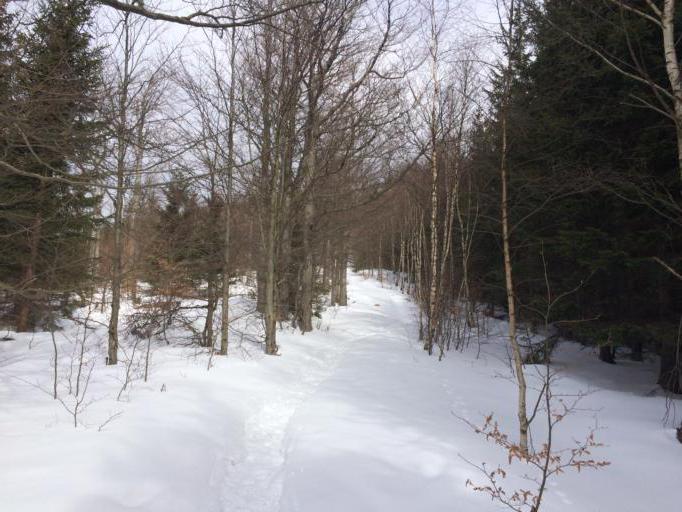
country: CZ
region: Olomoucky
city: Vapenna
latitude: 50.2616
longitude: 17.0111
